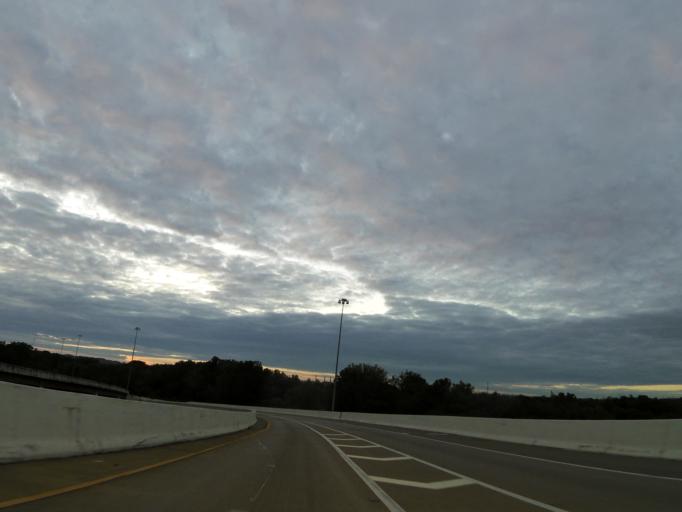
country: US
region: Tennessee
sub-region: Davidson County
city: Belle Meade
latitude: 36.1553
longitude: -86.8576
